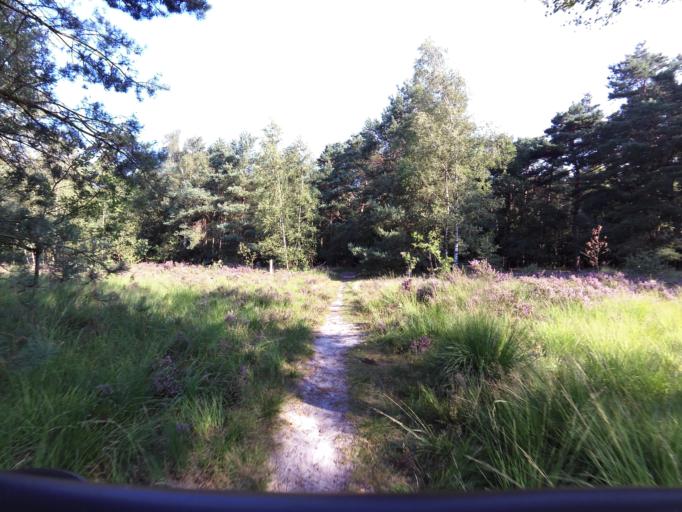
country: BE
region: Flanders
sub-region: Provincie Antwerpen
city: Kalmthout
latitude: 51.3729
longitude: 4.4528
